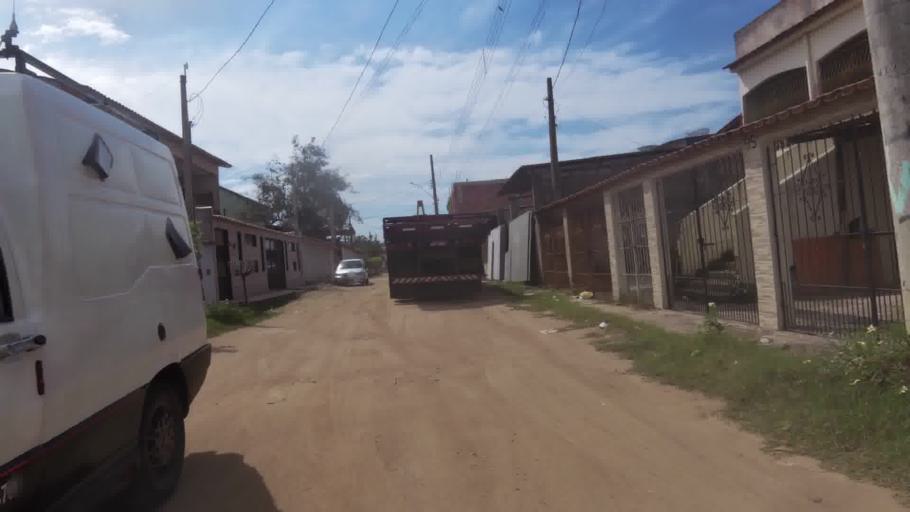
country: BR
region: Espirito Santo
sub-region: Piuma
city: Piuma
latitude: -20.8438
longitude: -40.7451
